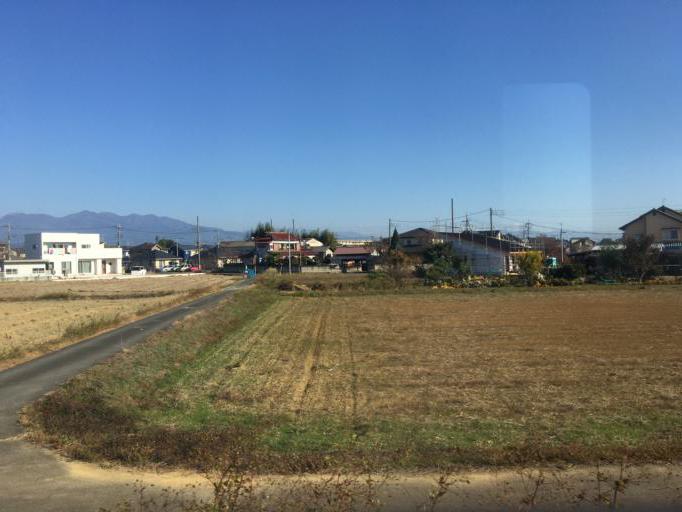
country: JP
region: Gunma
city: Maebashi-shi
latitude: 36.3654
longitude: 139.1189
